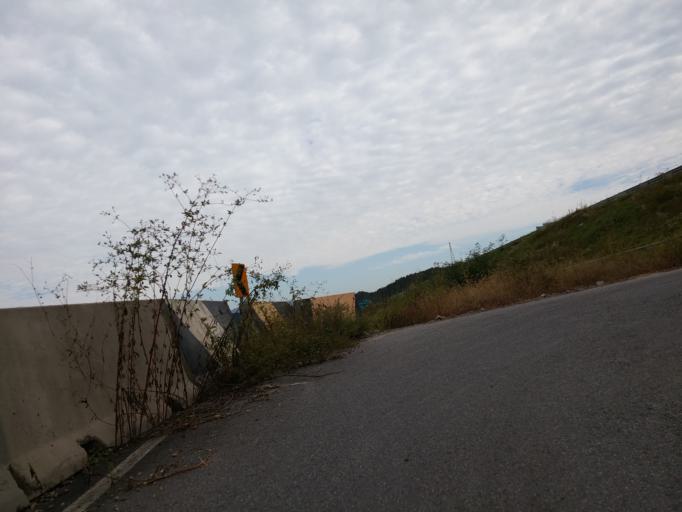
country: KR
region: Chungcheongnam-do
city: Yonmu
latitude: 36.1618
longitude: 127.2010
